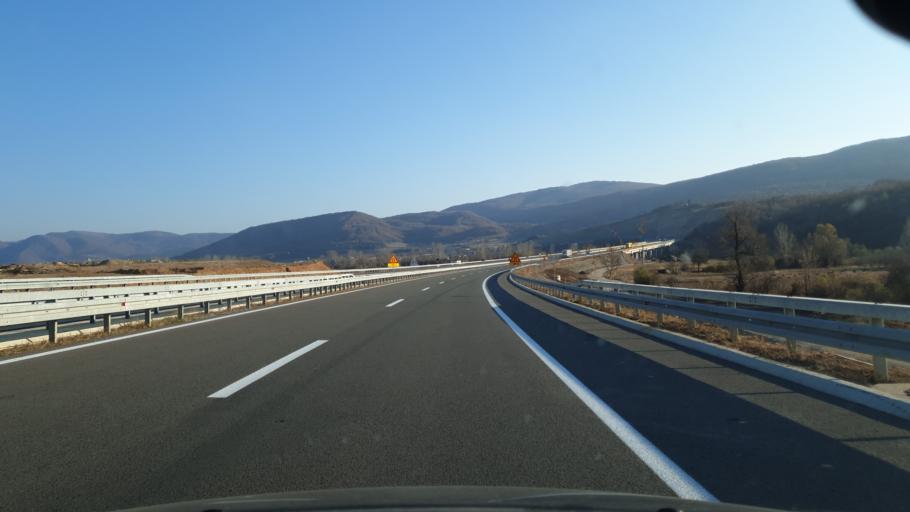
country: RS
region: Central Serbia
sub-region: Pirotski Okrug
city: Dimitrovgrad
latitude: 43.0154
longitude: 22.8012
